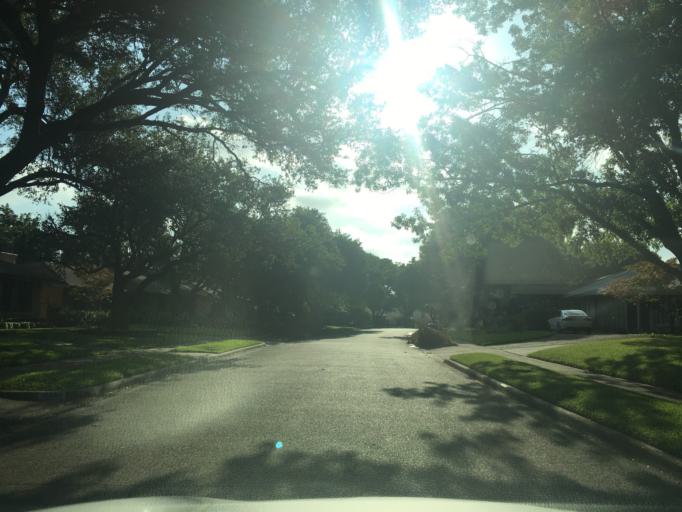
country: US
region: Texas
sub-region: Dallas County
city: Highland Park
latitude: 32.8460
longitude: -96.7586
